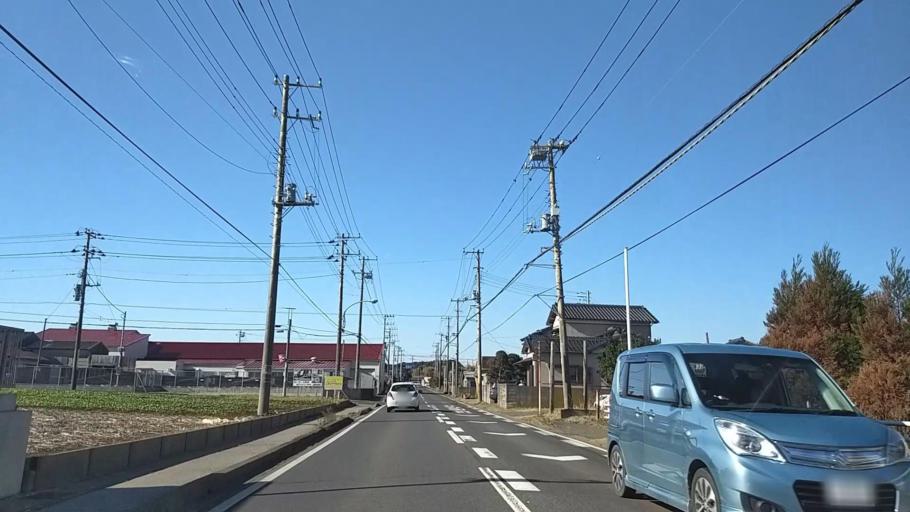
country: JP
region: Chiba
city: Hasaki
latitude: 35.7108
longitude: 140.7808
